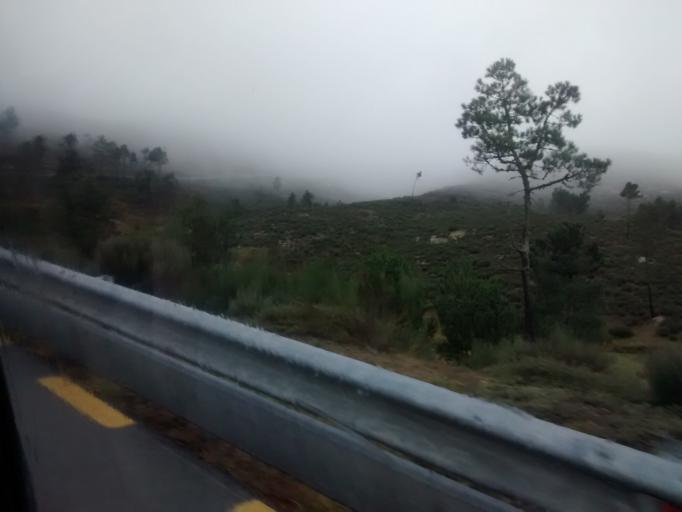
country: PT
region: Guarda
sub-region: Seia
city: Seia
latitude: 40.3991
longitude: -7.6501
